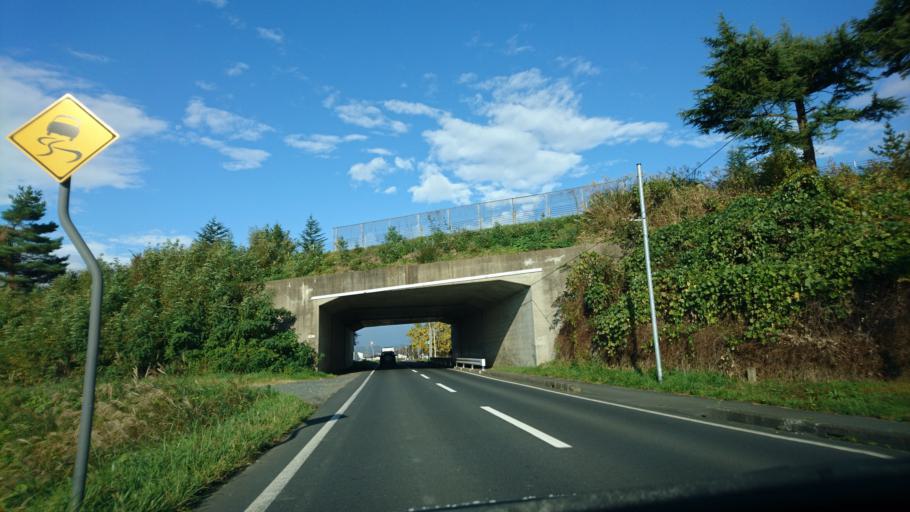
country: JP
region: Iwate
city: Ichinoseki
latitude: 39.0170
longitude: 141.1002
